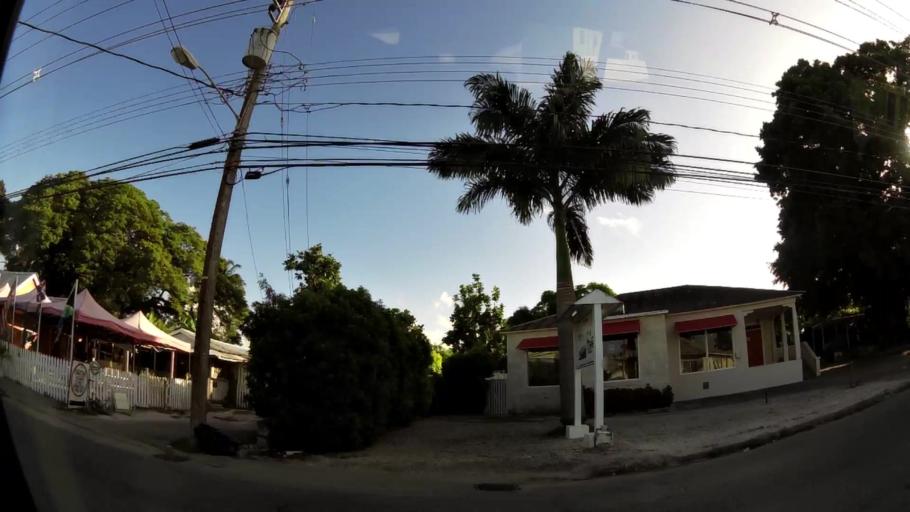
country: BB
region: Saint Michael
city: Bridgetown
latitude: 13.0849
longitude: -59.6086
